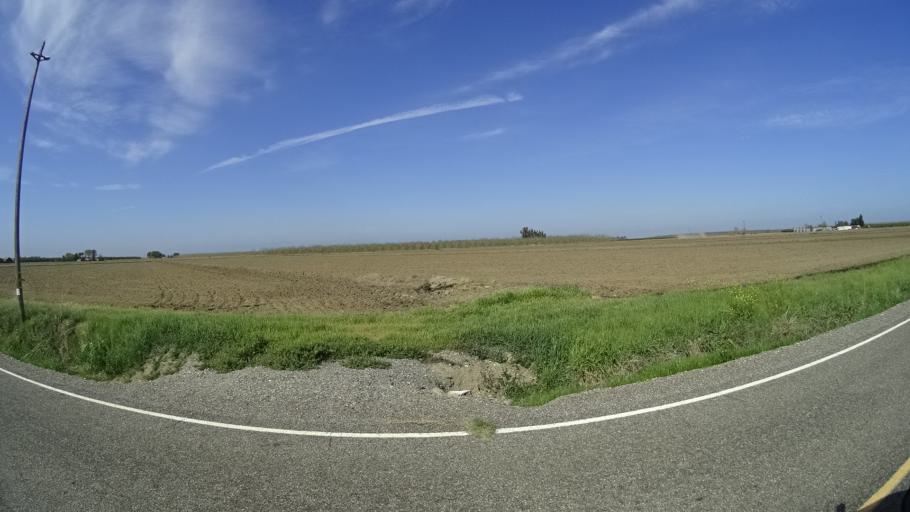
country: US
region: California
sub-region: Glenn County
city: Hamilton City
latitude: 39.6214
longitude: -122.0369
